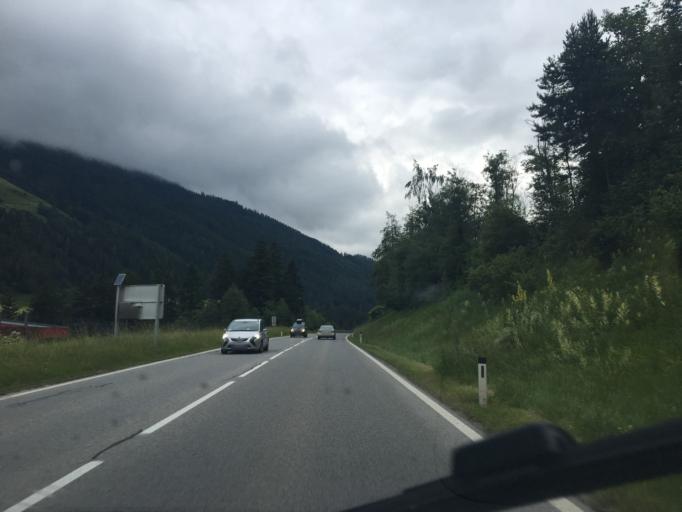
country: AT
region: Tyrol
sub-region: Politischer Bezirk Innsbruck Land
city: Neustift im Stubaital
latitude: 47.1344
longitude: 11.3409
